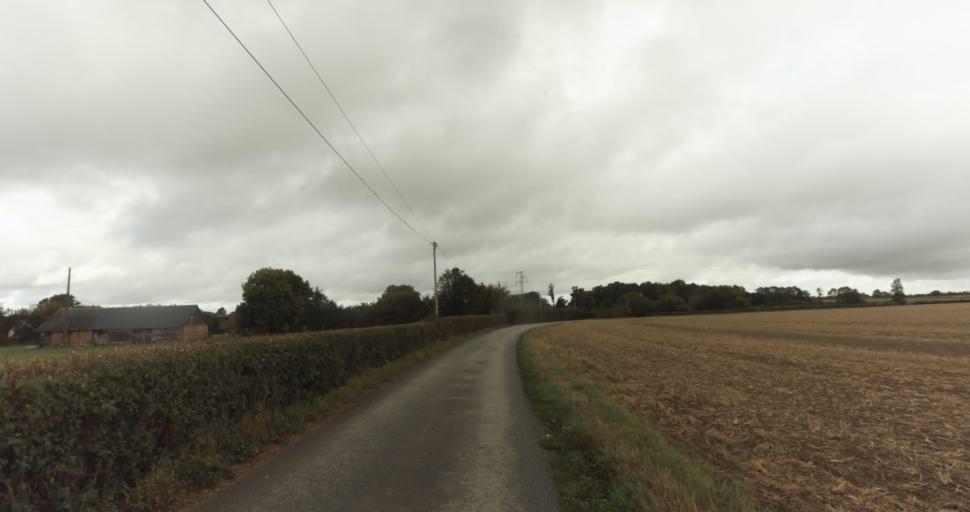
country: FR
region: Lower Normandy
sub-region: Departement de l'Orne
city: Gace
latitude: 48.8947
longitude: 0.3105
